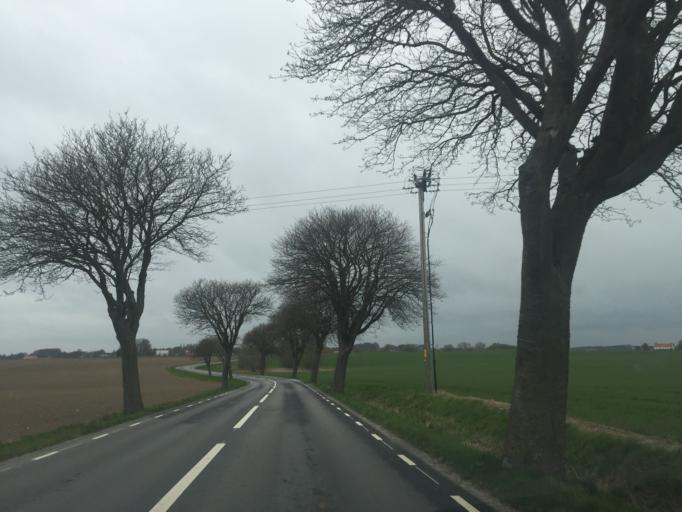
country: SE
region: Skane
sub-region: Skurups Kommun
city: Skivarp
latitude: 55.4240
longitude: 13.5982
